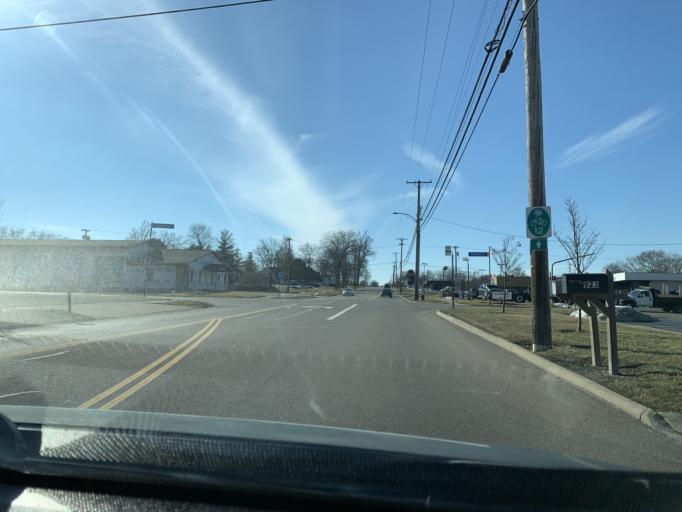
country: US
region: Ohio
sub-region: Montgomery County
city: Centerville
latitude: 39.6285
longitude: -84.1408
